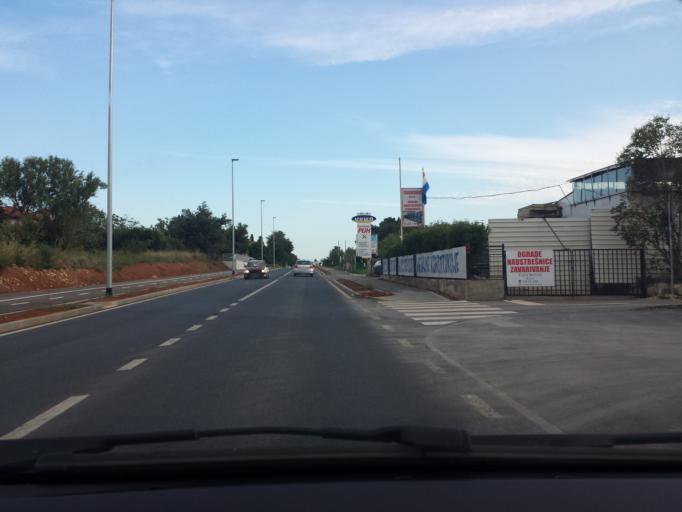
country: HR
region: Istarska
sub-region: Grad Pula
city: Pula
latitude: 44.8974
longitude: 13.8451
